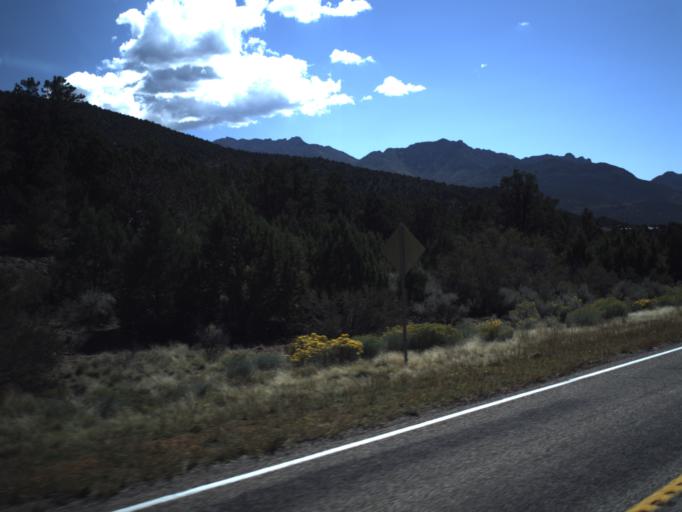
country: US
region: Utah
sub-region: Washington County
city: Enterprise
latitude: 37.4365
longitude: -113.6291
